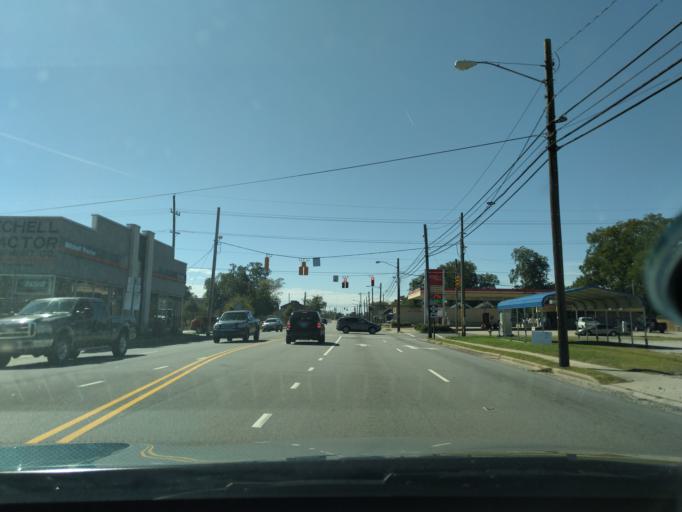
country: US
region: North Carolina
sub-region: Beaufort County
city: Washington
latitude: 35.5475
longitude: -77.0591
